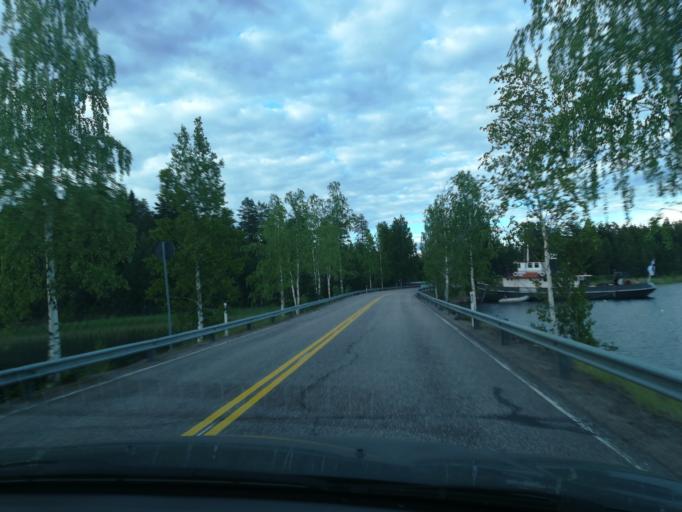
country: FI
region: Southern Savonia
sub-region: Mikkeli
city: Puumala
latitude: 61.5627
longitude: 27.9889
